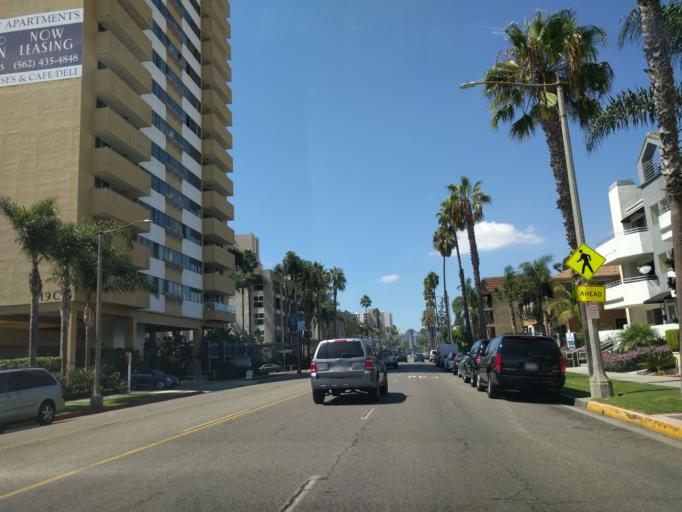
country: US
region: California
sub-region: Los Angeles County
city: Long Beach
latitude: 33.7646
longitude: -118.1689
